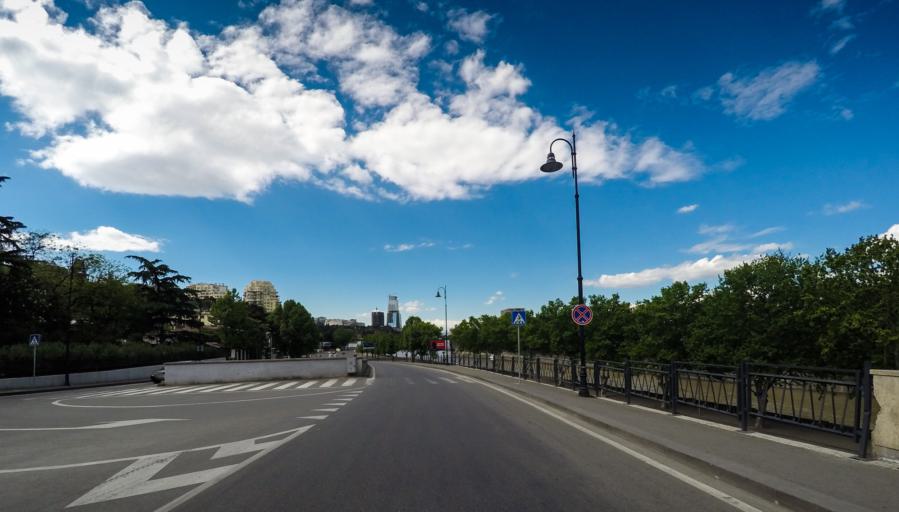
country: GE
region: T'bilisi
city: Tbilisi
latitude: 41.7075
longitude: 44.7915
